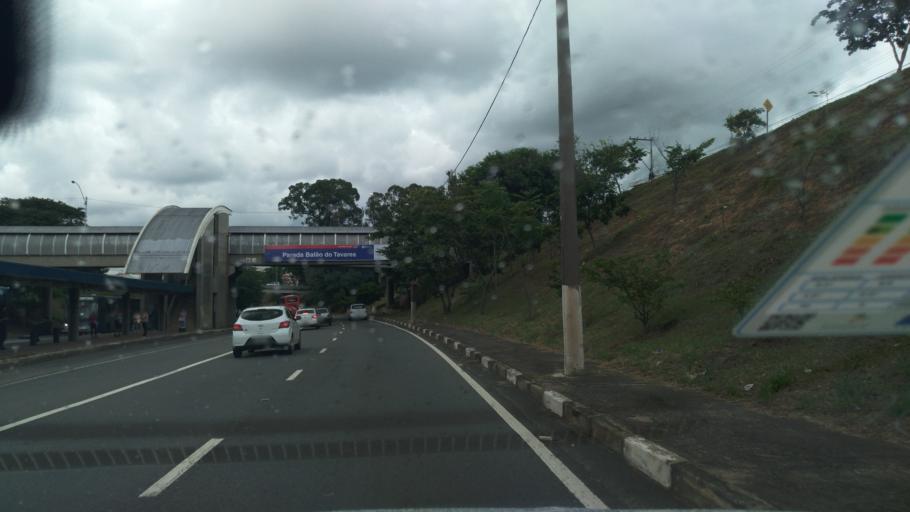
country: BR
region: Sao Paulo
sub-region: Campinas
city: Campinas
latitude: -22.8969
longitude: -47.0952
